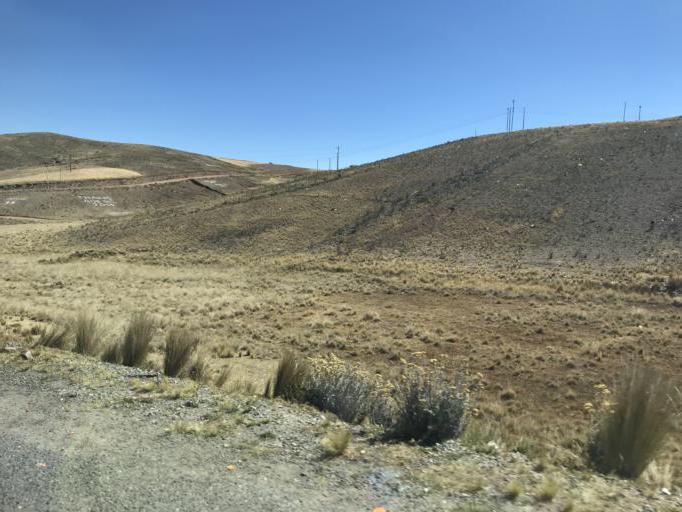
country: BO
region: La Paz
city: Tiahuanaco
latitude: -16.5785
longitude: -68.5350
